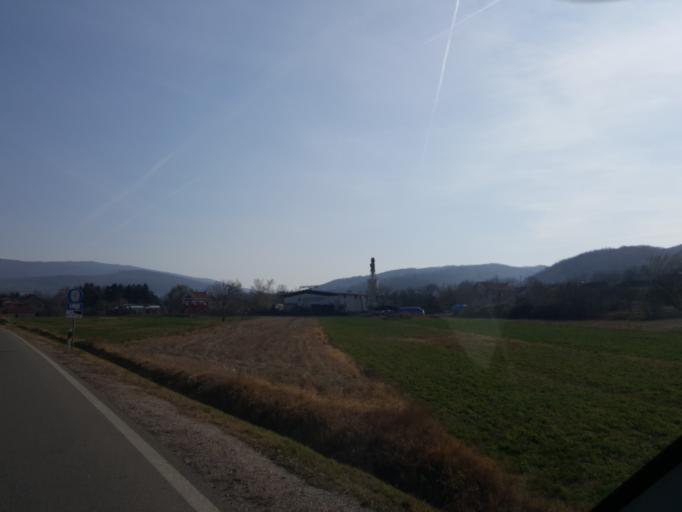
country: RS
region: Central Serbia
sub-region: Pomoravski Okrug
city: Paracin
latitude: 43.8561
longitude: 21.5545
